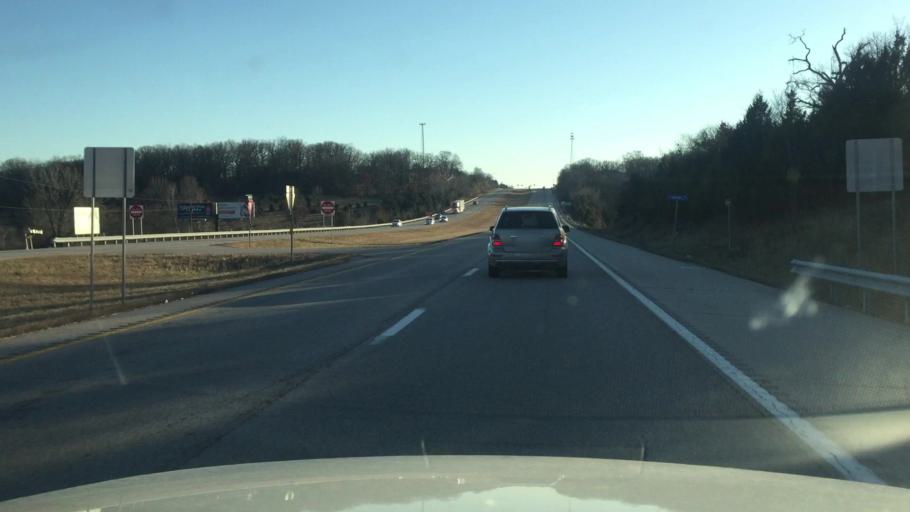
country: US
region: Missouri
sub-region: Cole County
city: Wardsville
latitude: 38.4911
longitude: -92.2702
